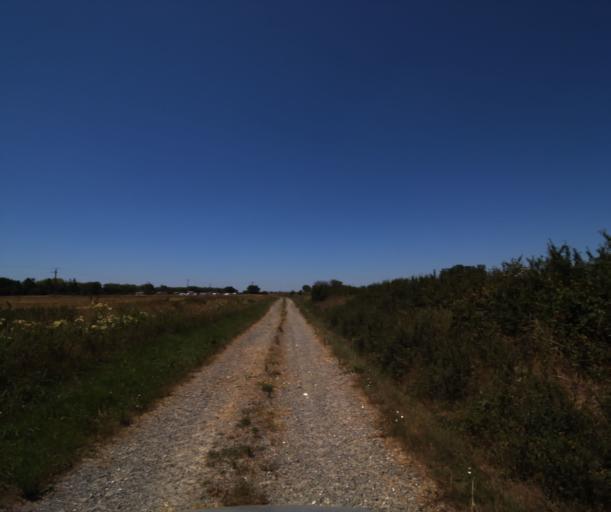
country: FR
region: Midi-Pyrenees
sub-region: Departement de la Haute-Garonne
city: Seysses
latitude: 43.4673
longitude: 1.2987
